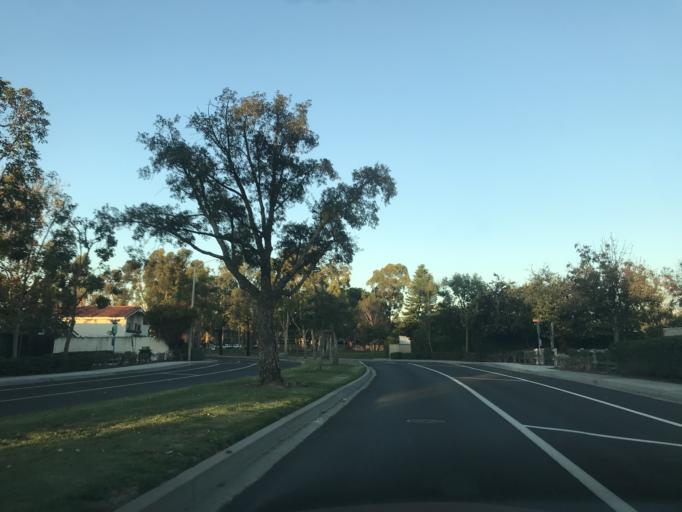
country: US
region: California
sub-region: Orange County
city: North Tustin
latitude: 33.7090
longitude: -117.7606
